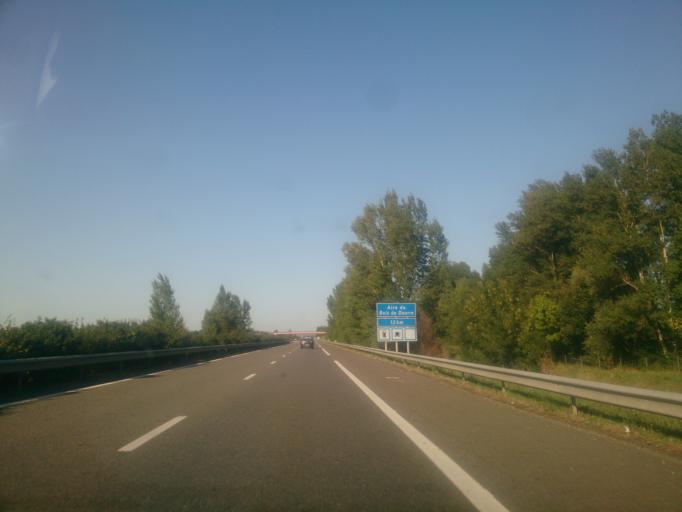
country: FR
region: Midi-Pyrenees
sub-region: Departement du Tarn-et-Garonne
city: Realville
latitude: 44.1335
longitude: 1.4886
